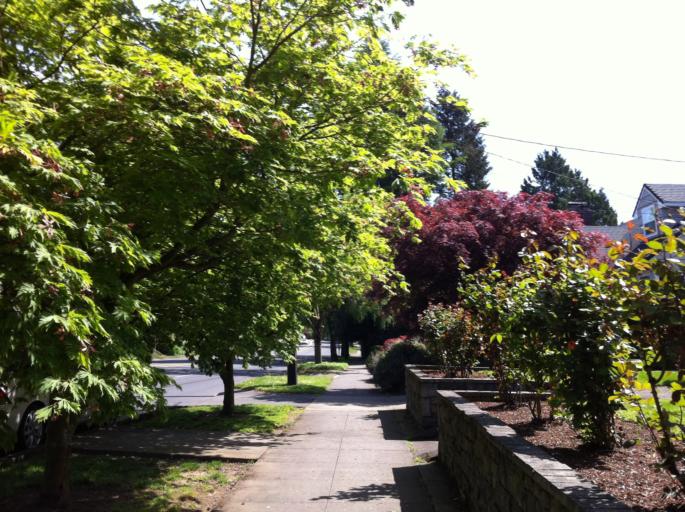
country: US
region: Oregon
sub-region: Multnomah County
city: Portland
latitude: 45.5228
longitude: -122.6301
